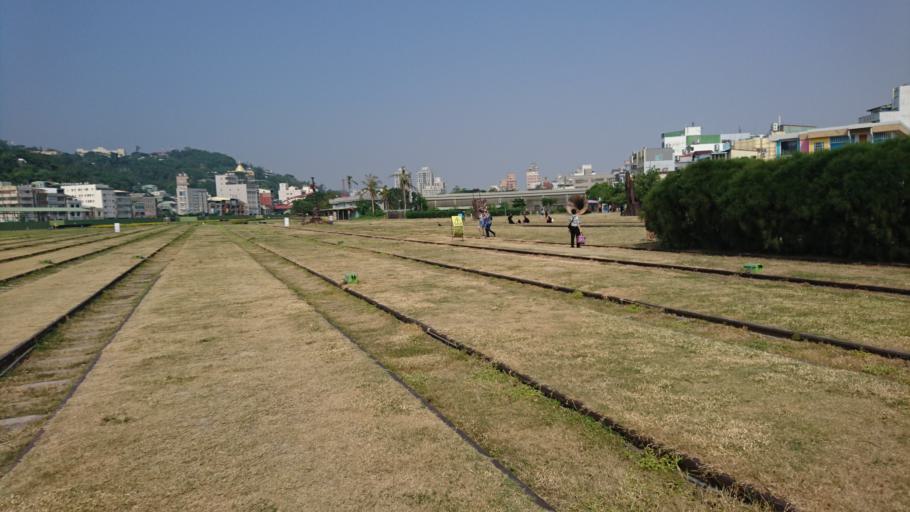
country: TW
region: Kaohsiung
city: Kaohsiung
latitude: 22.6207
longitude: 120.2768
